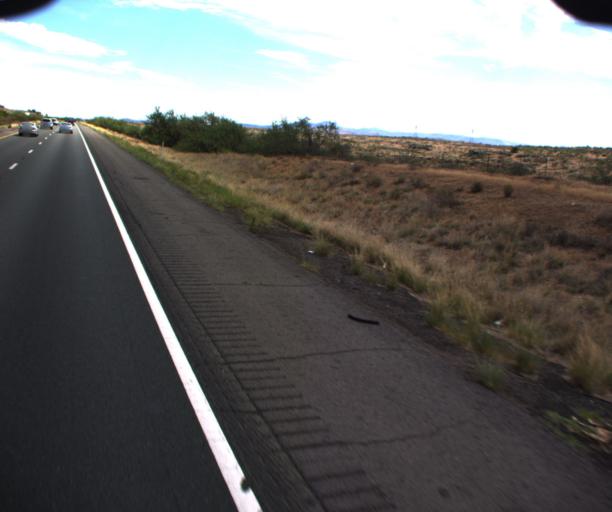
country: US
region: Arizona
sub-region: Yavapai County
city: Spring Valley
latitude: 34.3687
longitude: -112.1122
